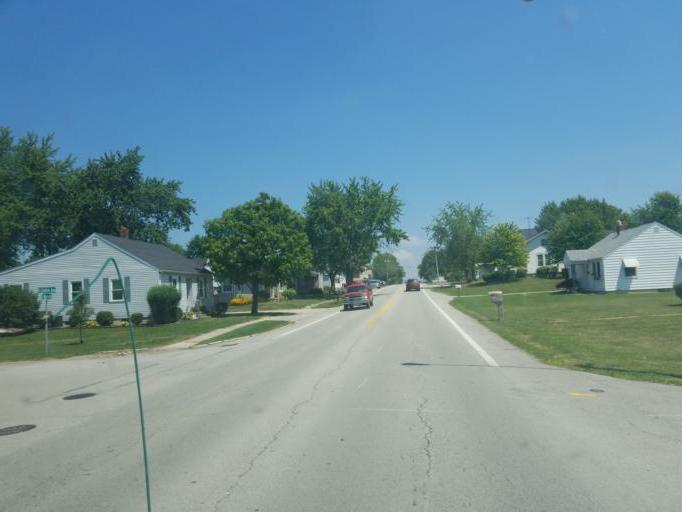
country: US
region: Ohio
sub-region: Shelby County
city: Anna
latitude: 40.3951
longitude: -84.1720
